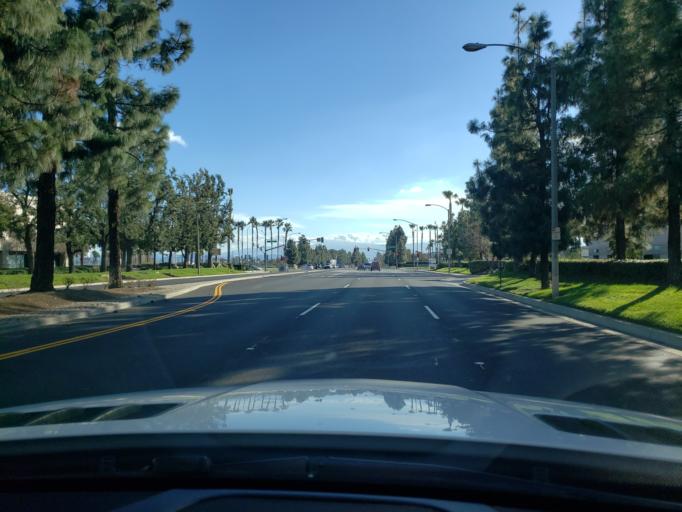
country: US
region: California
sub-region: San Bernardino County
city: Rancho Cucamonga
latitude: 34.0495
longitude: -117.5584
